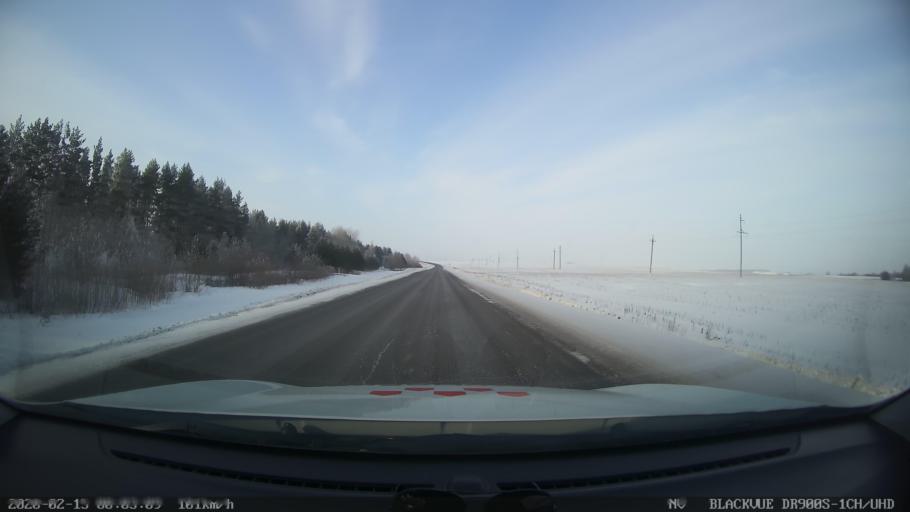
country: RU
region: Tatarstan
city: Kuybyshevskiy Zaton
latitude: 55.3679
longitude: 48.9996
